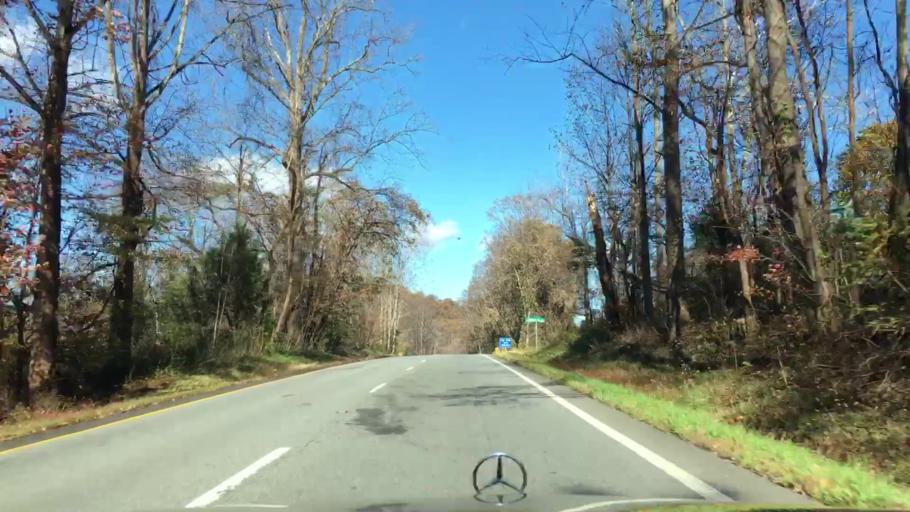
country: US
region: Virginia
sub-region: Nelson County
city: Nellysford
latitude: 37.8771
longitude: -78.7152
